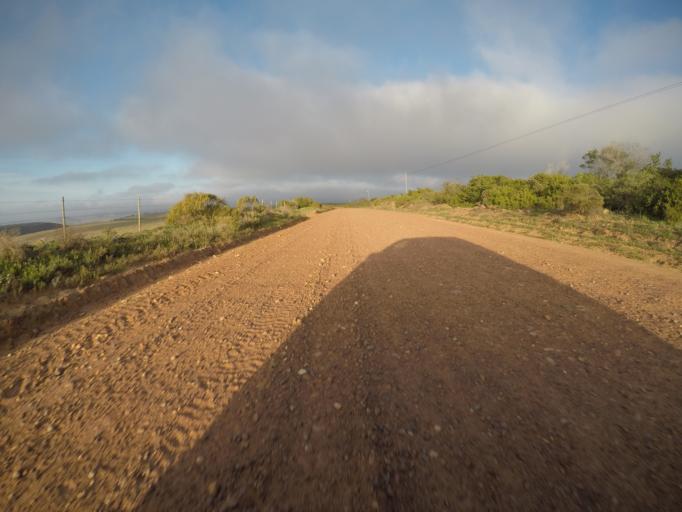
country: ZA
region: Western Cape
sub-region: Eden District Municipality
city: Mossel Bay
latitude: -34.1428
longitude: 22.0297
